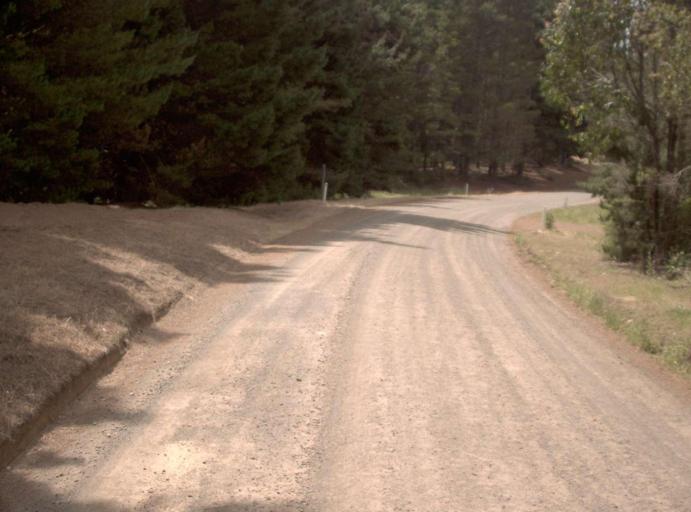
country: AU
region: Victoria
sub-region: Latrobe
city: Traralgon
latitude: -38.3834
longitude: 146.6651
